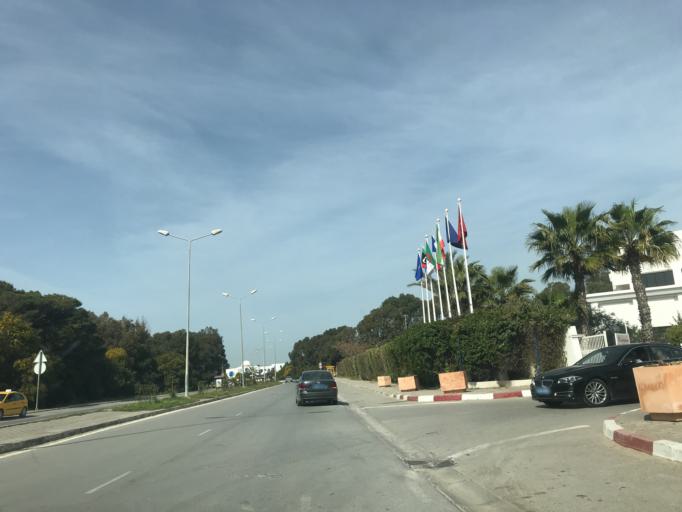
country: TN
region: Tunis
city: Al Marsa
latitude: 36.9205
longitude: 10.2883
